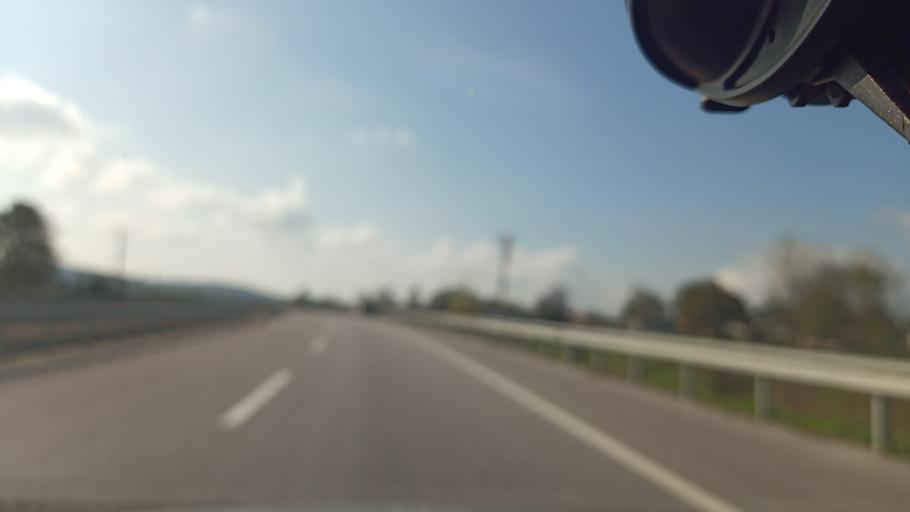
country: TR
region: Sakarya
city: Kaynarca
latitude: 41.0333
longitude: 30.3277
